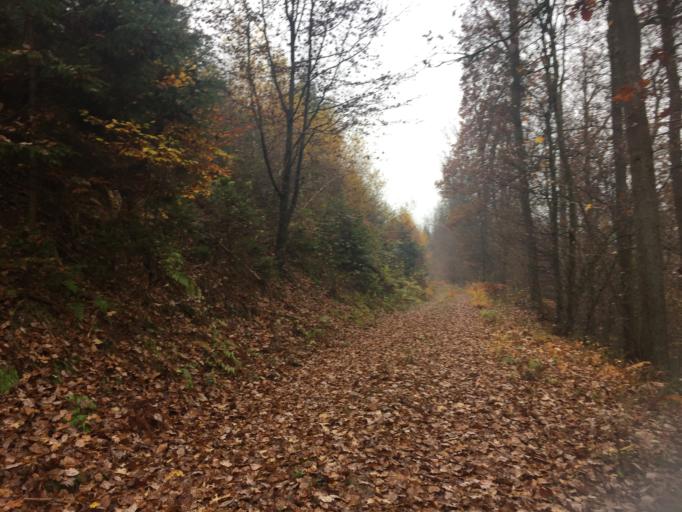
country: DE
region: Hesse
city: Hirschhorn
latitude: 49.4588
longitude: 8.8677
